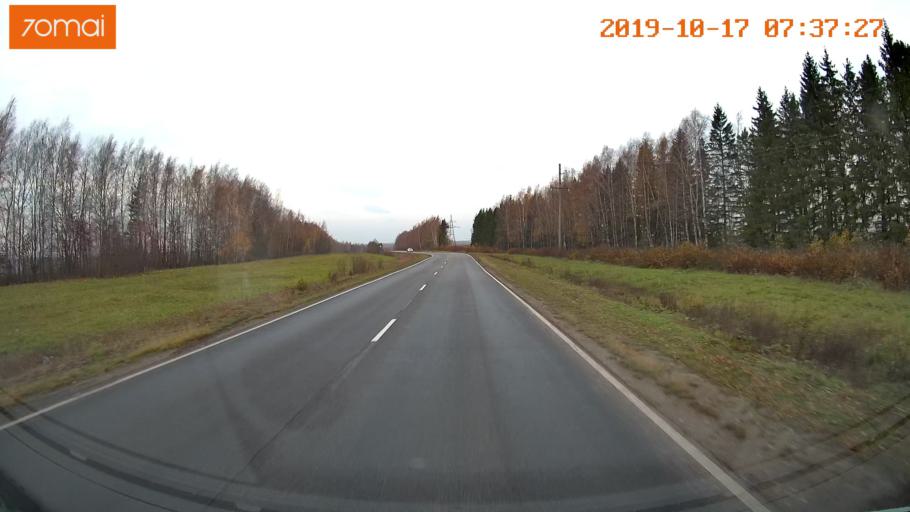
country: RU
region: Vladimir
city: Yur'yev-Pol'skiy
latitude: 56.4494
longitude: 39.8990
